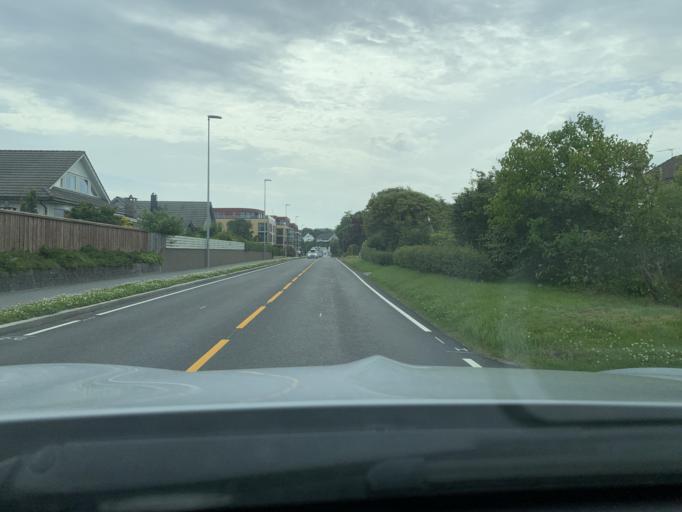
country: NO
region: Rogaland
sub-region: Sandnes
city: Sandnes
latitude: 58.7809
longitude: 5.7187
